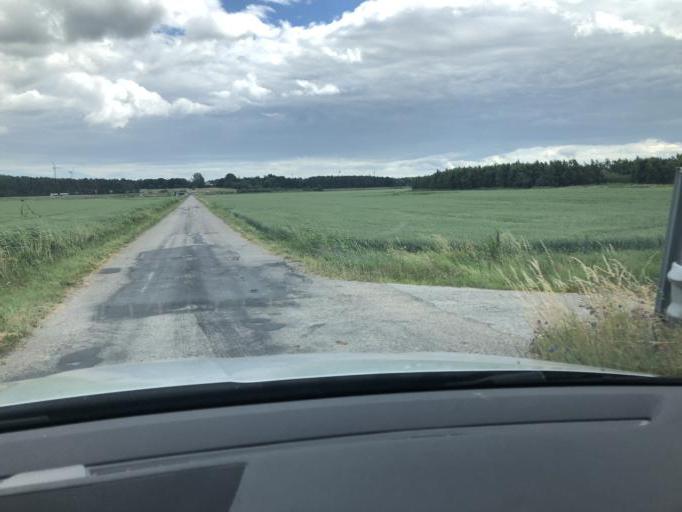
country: SE
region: Blekinge
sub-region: Solvesborgs Kommun
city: Soelvesborg
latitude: 56.0966
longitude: 14.6354
